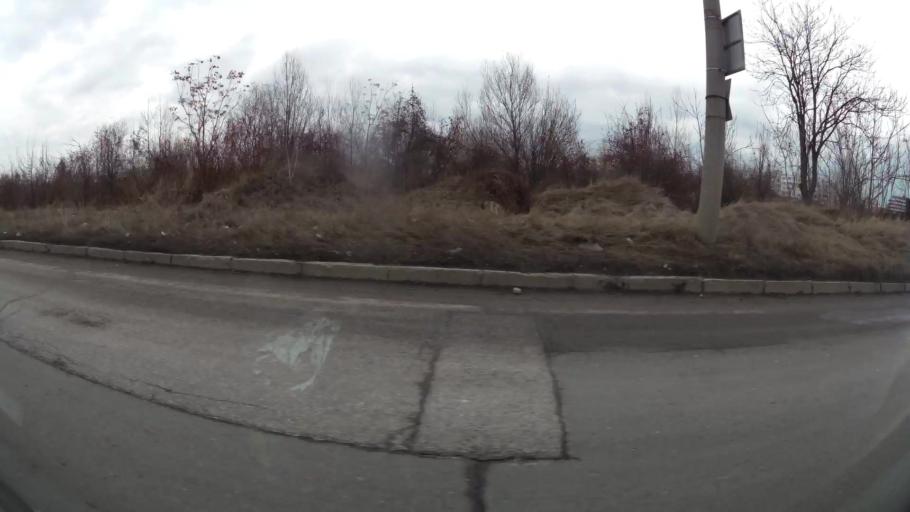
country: BG
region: Sofiya
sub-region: Obshtina Bozhurishte
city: Bozhurishte
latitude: 42.7365
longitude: 23.2647
